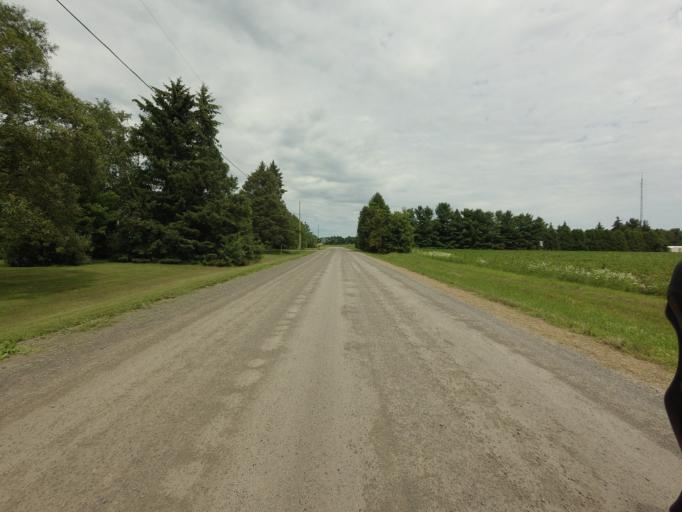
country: CA
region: Ontario
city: Bells Corners
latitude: 45.0838
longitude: -75.5966
